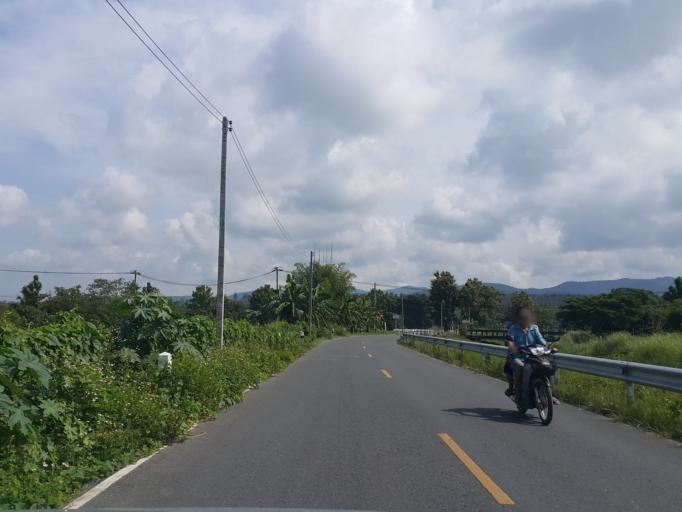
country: TH
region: Chiang Mai
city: San Sai
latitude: 18.9568
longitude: 98.9905
